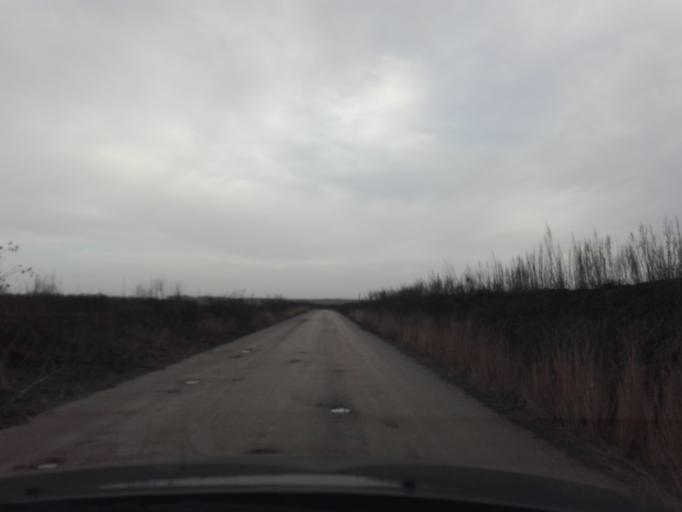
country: AT
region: Upper Austria
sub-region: Politischer Bezirk Linz-Land
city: Horsching
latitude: 48.2181
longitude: 14.1542
